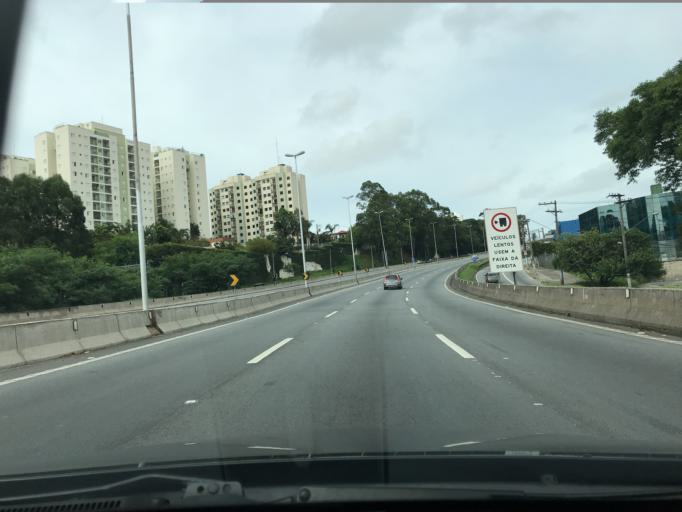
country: BR
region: Sao Paulo
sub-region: Taboao Da Serra
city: Taboao da Serra
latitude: -23.5849
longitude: -46.7385
